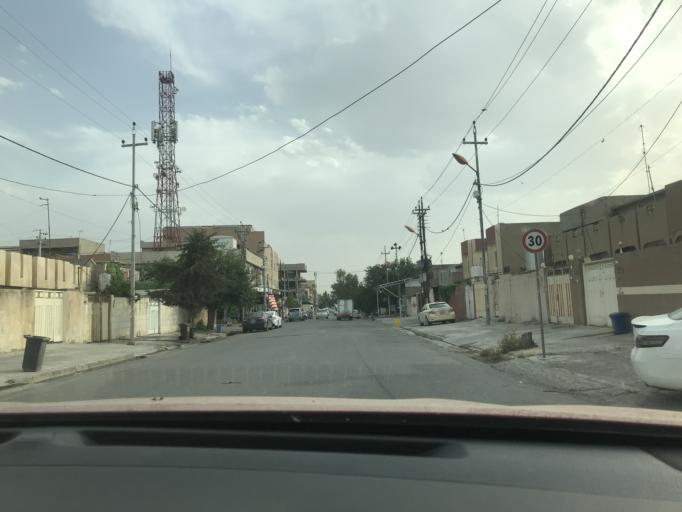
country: IQ
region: Arbil
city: Erbil
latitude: 36.1783
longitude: 43.9768
